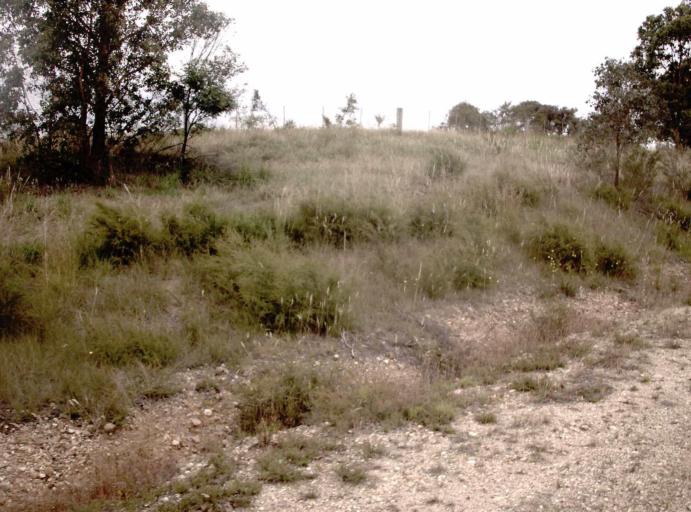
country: AU
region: Victoria
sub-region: East Gippsland
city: Bairnsdale
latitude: -37.7954
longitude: 147.3666
